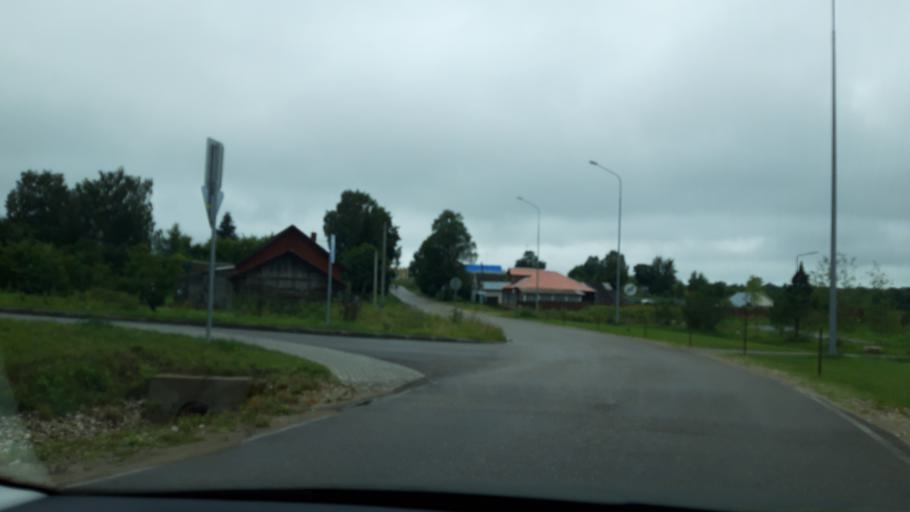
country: RU
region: Tverskaya
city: Zavidovo
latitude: 56.5808
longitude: 36.5204
